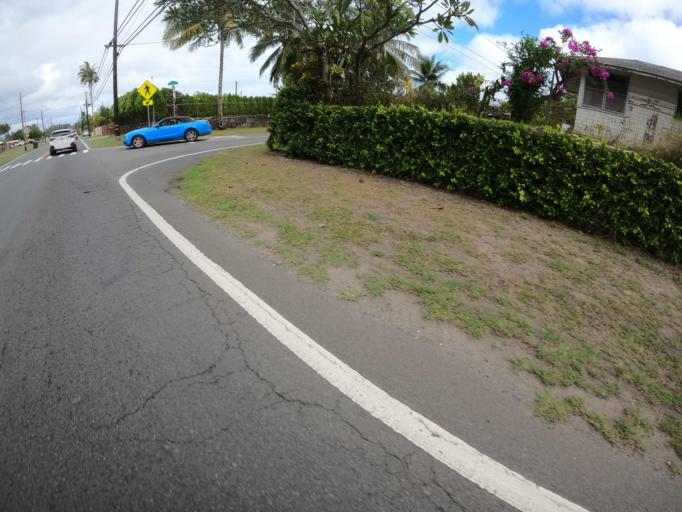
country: US
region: Hawaii
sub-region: Honolulu County
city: Waimanalo Beach
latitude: 21.3345
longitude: -157.6988
